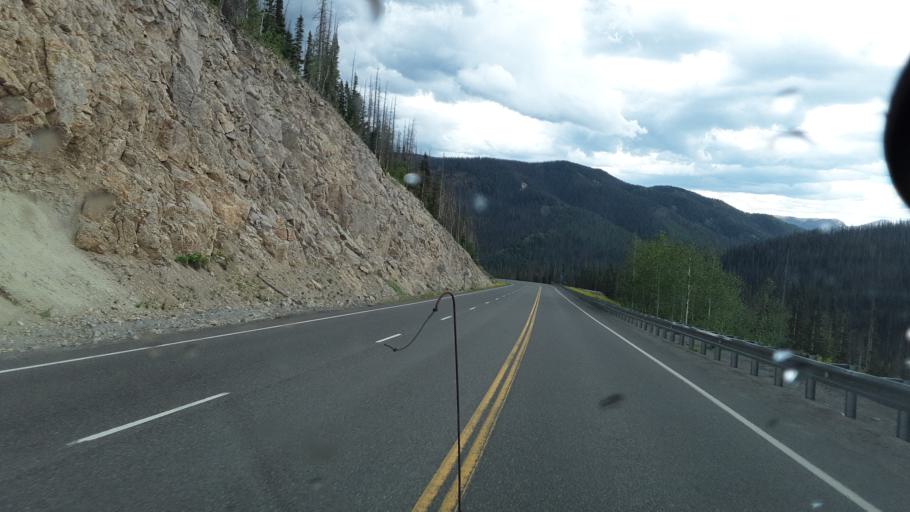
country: US
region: Colorado
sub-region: Archuleta County
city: Pagosa Springs
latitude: 37.4796
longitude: -106.7762
